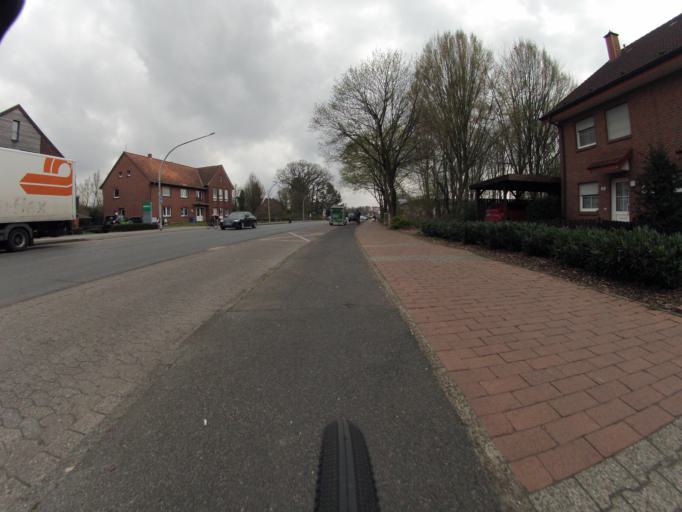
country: DE
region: North Rhine-Westphalia
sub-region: Regierungsbezirk Munster
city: Recke
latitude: 52.3648
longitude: 7.7193
